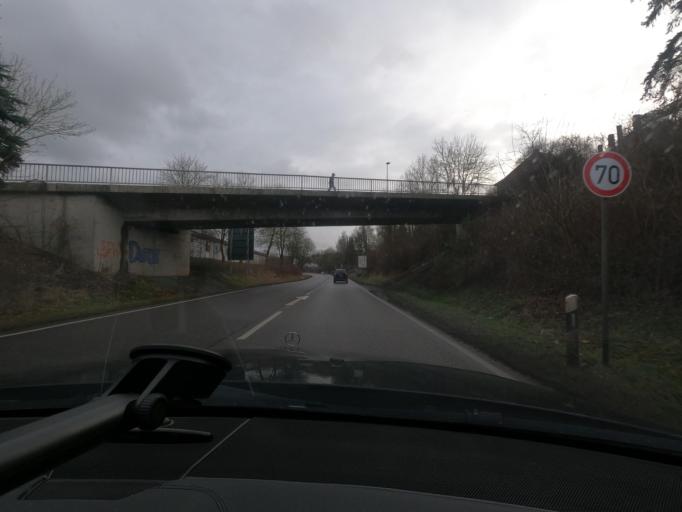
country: DE
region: Hesse
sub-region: Regierungsbezirk Kassel
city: Wolfhagen
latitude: 51.3278
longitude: 9.1766
